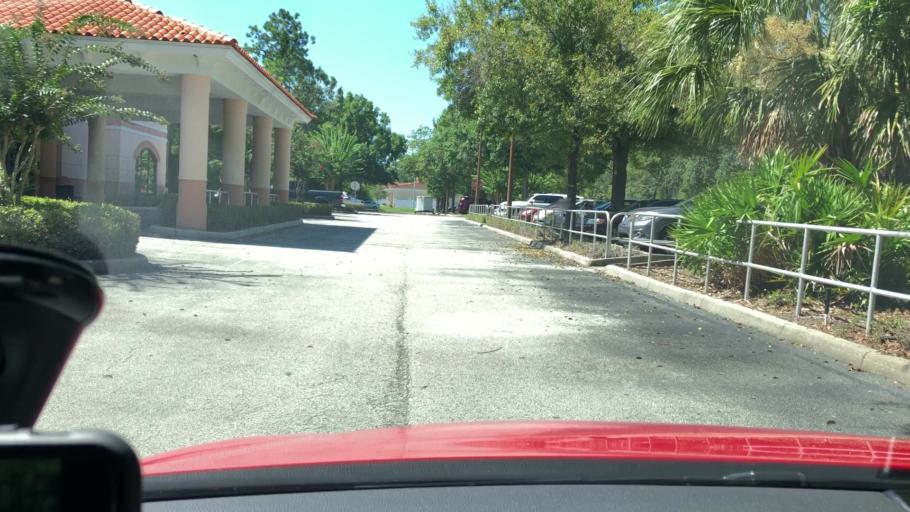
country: US
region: Florida
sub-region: Volusia County
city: Ormond Beach
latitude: 29.2551
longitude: -81.1202
